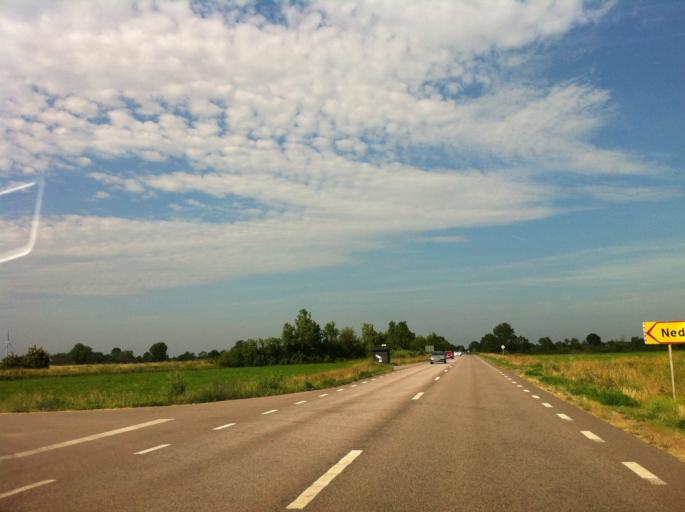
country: SE
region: Kalmar
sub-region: Borgholms Kommun
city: Borgholm
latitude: 56.9124
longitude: 16.7409
